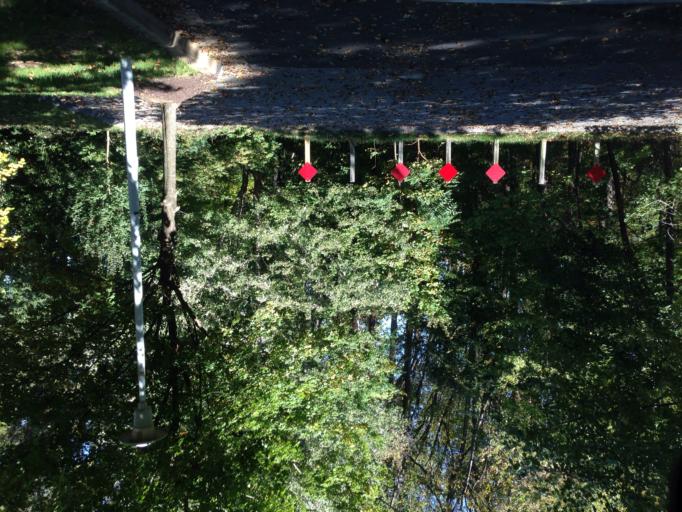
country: US
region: Maryland
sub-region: Howard County
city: Riverside
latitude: 39.1503
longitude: -76.8934
